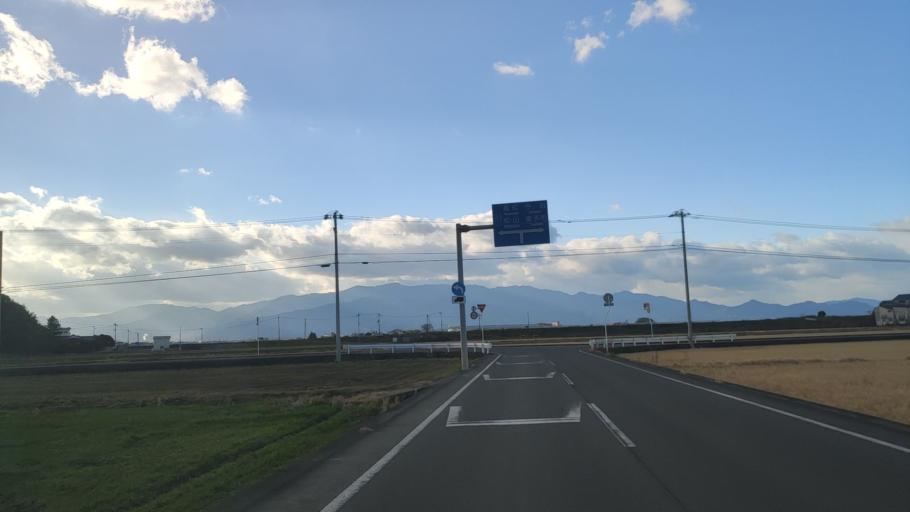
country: JP
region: Ehime
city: Saijo
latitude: 33.9043
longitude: 133.1299
